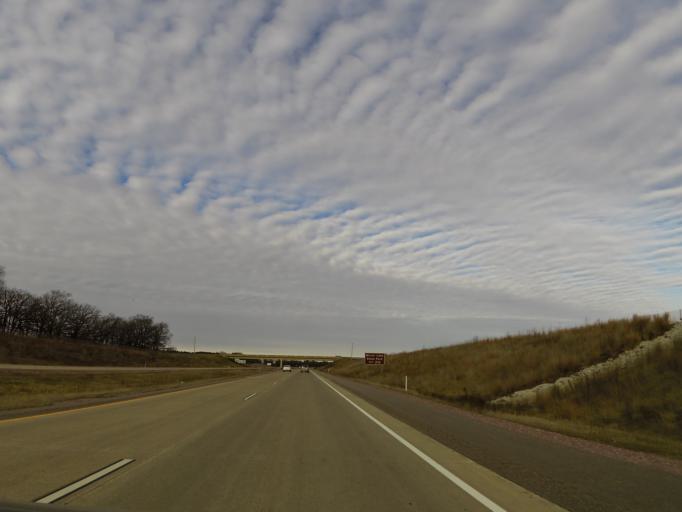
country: US
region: Wisconsin
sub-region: Sauk County
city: Lake Delton
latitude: 43.5442
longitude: -89.7870
